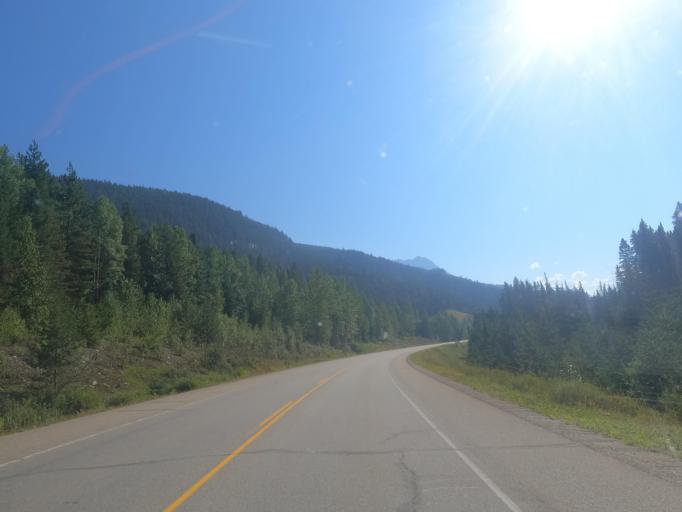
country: CA
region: Alberta
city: Jasper Park Lodge
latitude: 52.8928
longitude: -118.7354
